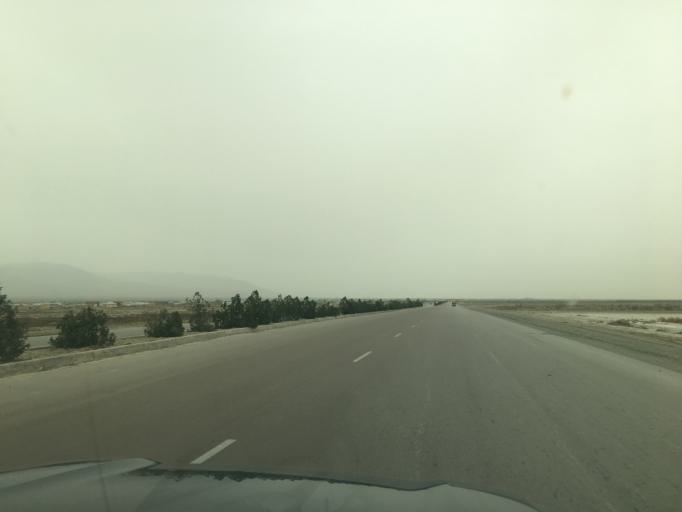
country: TM
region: Ahal
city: Baharly
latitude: 38.3749
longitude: 57.5108
